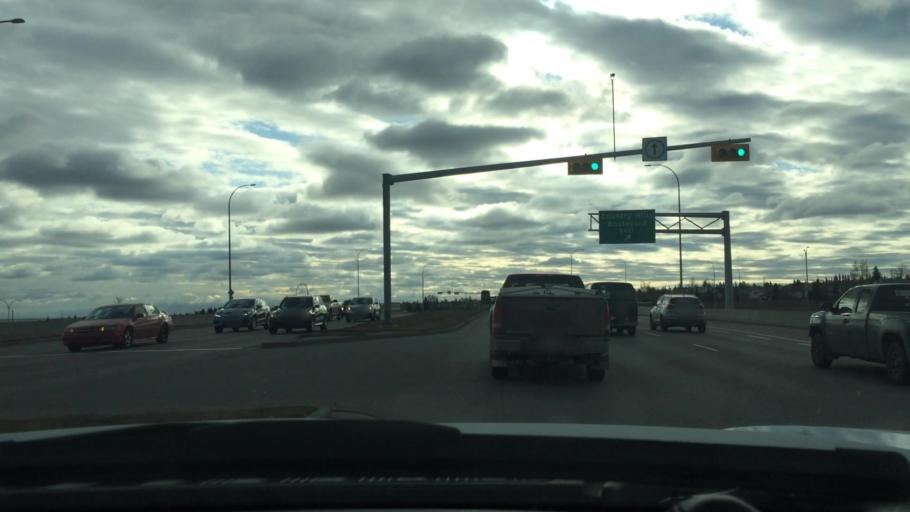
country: CA
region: Alberta
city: Calgary
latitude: 51.1449
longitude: -114.0936
